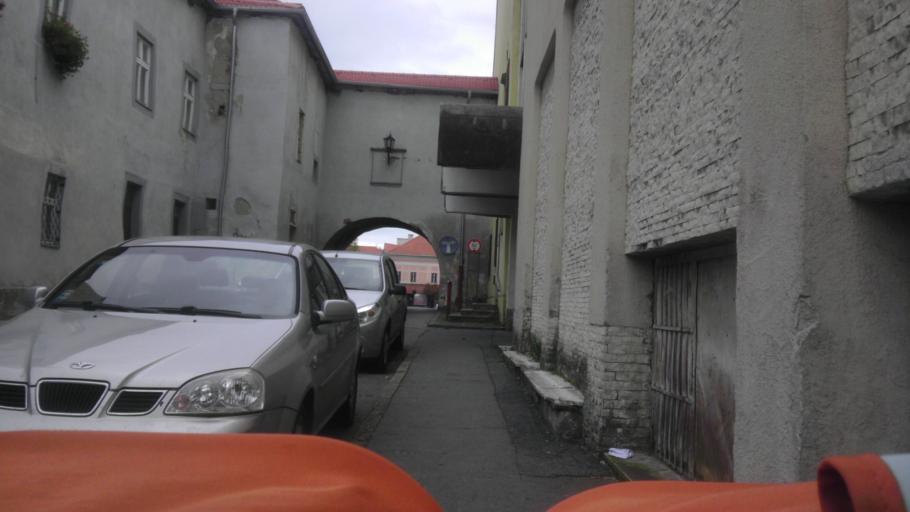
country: SK
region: Presovsky
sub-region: Okres Presov
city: Levoca
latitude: 49.0279
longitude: 20.5889
